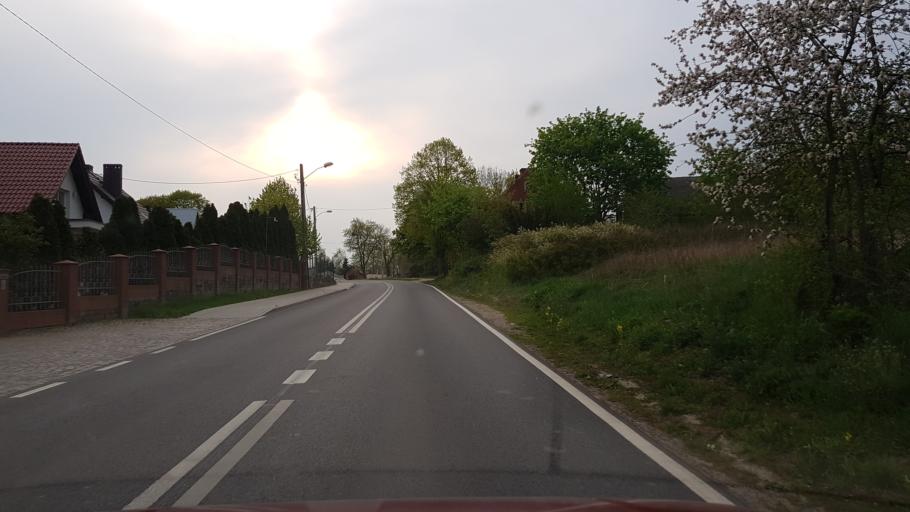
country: PL
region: West Pomeranian Voivodeship
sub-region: Powiat pyrzycki
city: Bielice
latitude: 53.2737
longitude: 14.6773
